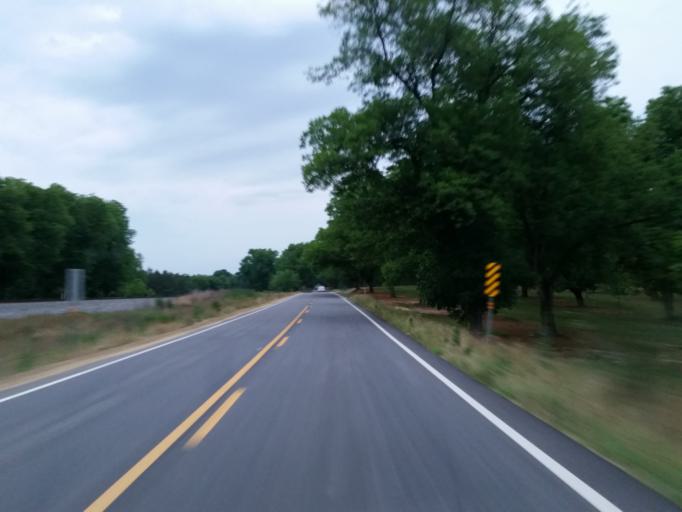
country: US
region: Georgia
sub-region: Turner County
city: Ashburn
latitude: 31.7889
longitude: -83.7049
